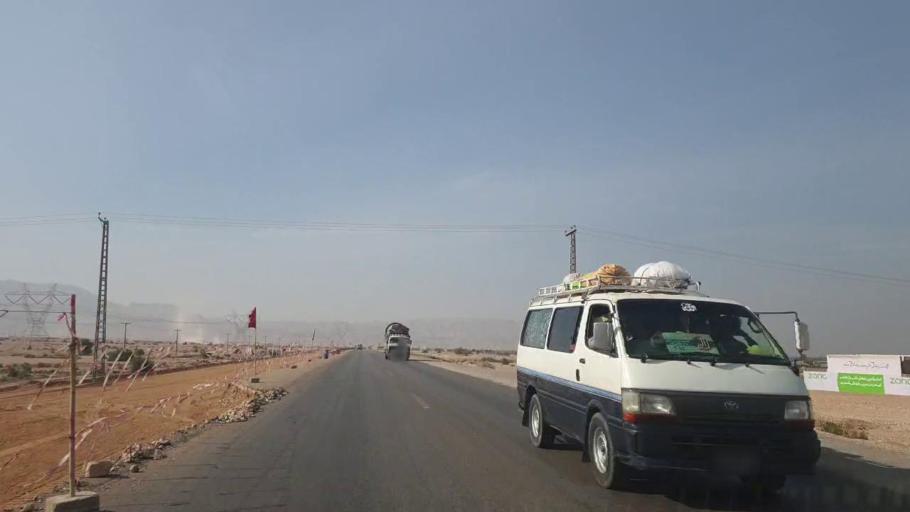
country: PK
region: Sindh
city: Sehwan
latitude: 26.2042
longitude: 67.9330
